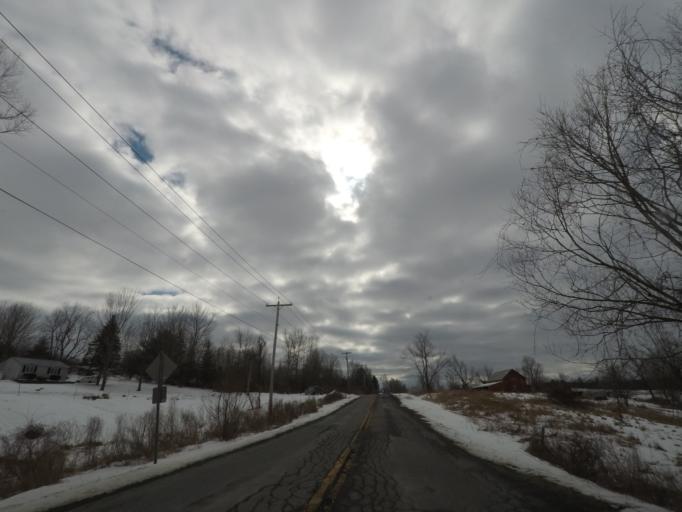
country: US
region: New York
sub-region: Rensselaer County
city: Hoosick Falls
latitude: 42.9286
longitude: -73.4340
